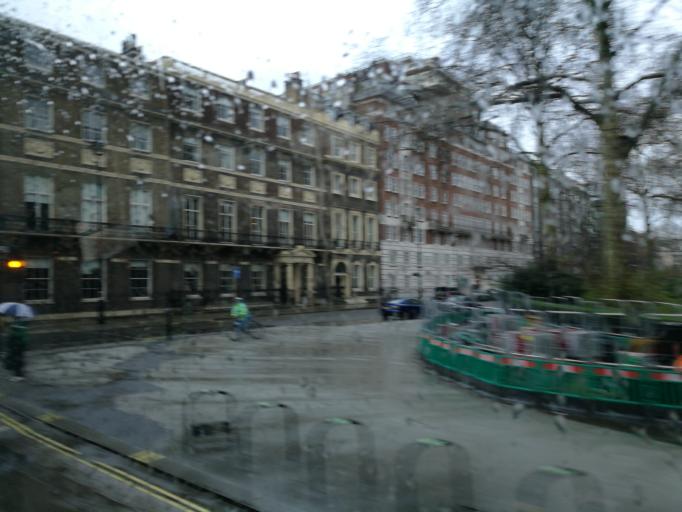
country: GB
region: England
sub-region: Greater London
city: Bayswater
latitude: 51.5157
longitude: -0.1567
